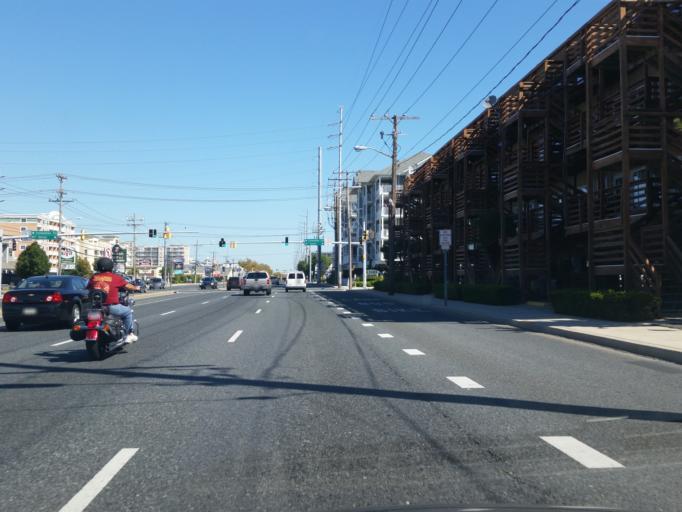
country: US
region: Maryland
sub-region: Worcester County
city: Ocean City
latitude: 38.3673
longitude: -75.0713
